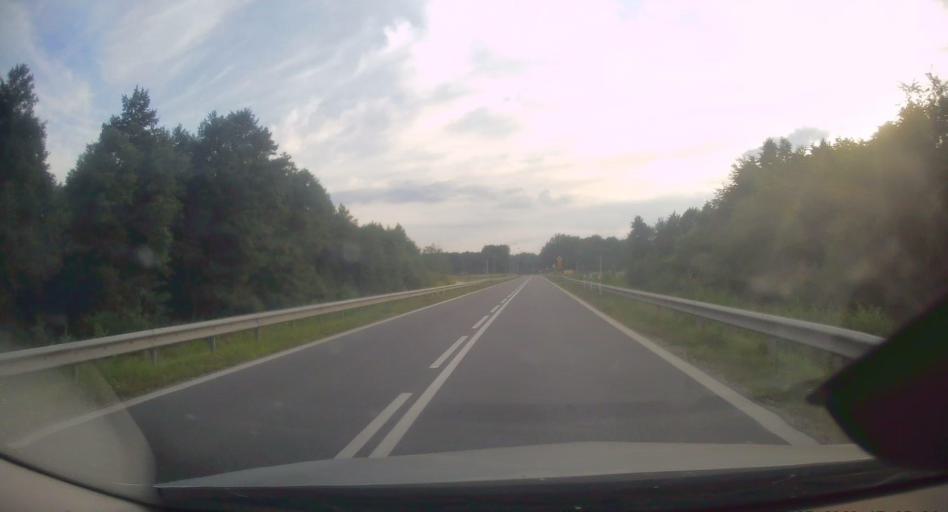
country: PL
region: Lesser Poland Voivodeship
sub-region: Powiat brzeski
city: Brzesko
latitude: 50.0083
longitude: 20.6088
